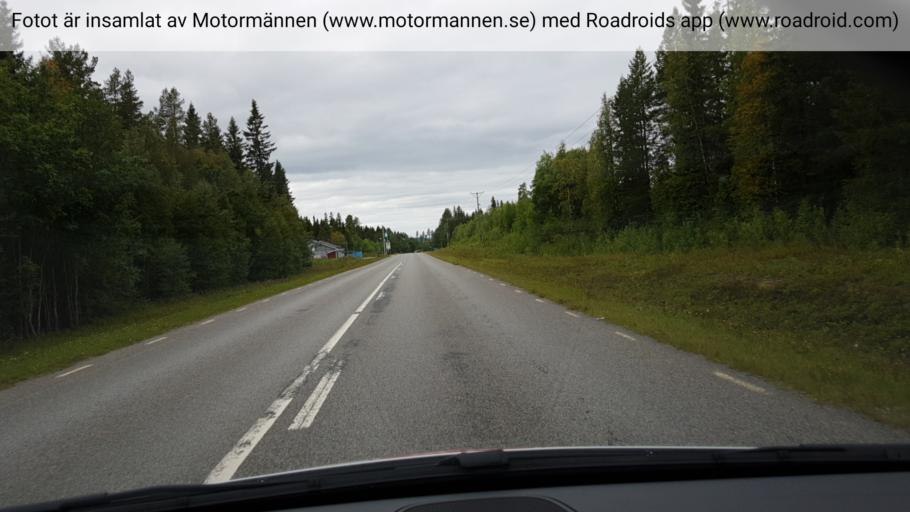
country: SE
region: Jaemtland
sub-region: Stroemsunds Kommun
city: Stroemsund
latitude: 64.3078
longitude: 15.2418
